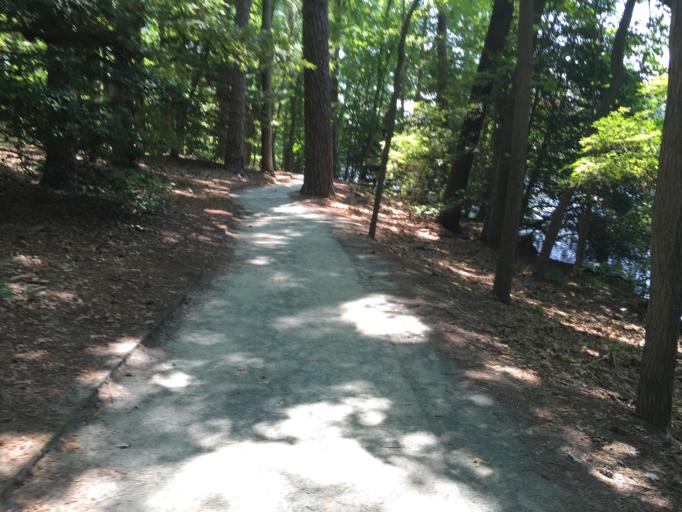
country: US
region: Virginia
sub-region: City of Newport News
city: Newport News
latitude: 37.0572
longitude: -76.4865
